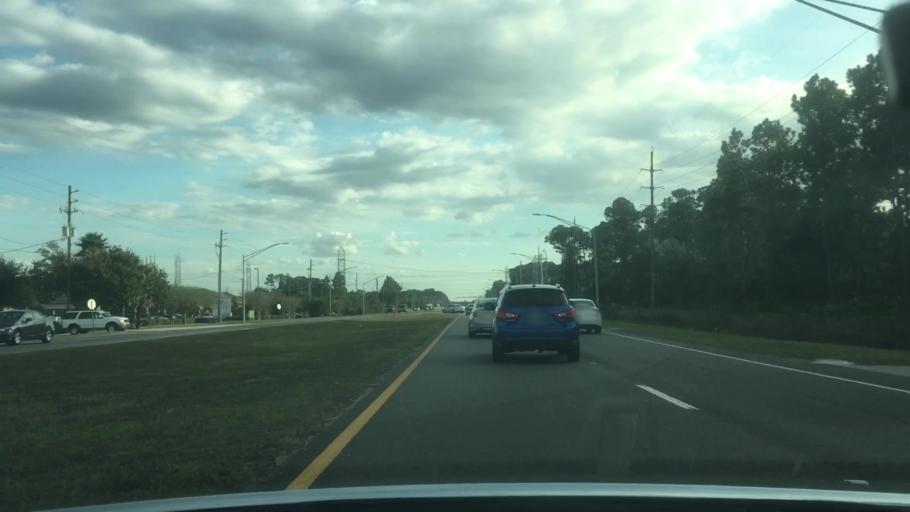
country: US
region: Florida
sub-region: Duval County
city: Neptune Beach
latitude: 30.3057
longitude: -81.5261
